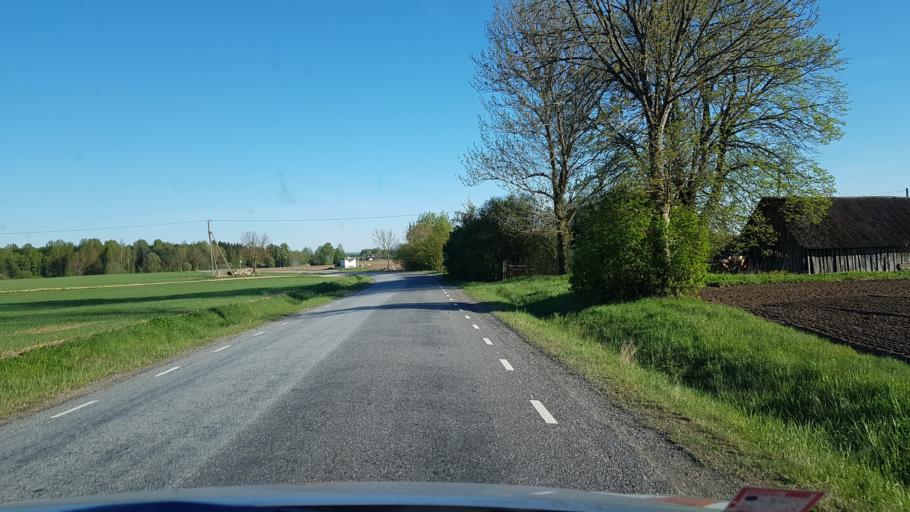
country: EE
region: Vorumaa
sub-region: Voru linn
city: Voru
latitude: 57.9198
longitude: 26.9518
